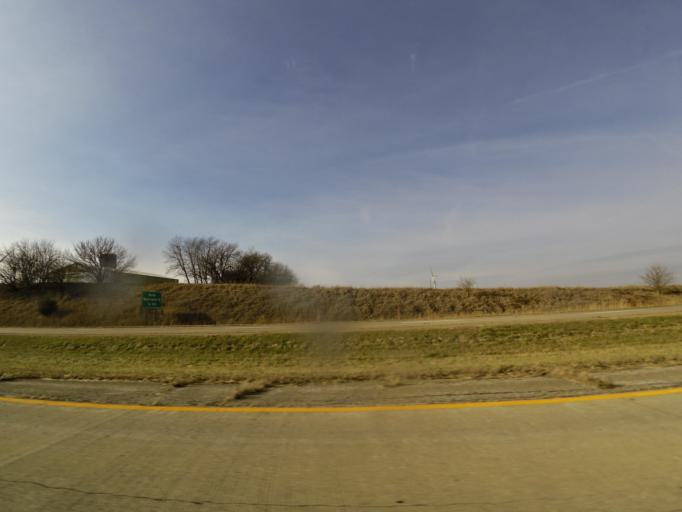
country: US
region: Illinois
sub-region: Macon County
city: Maroa
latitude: 40.0410
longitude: -88.9653
